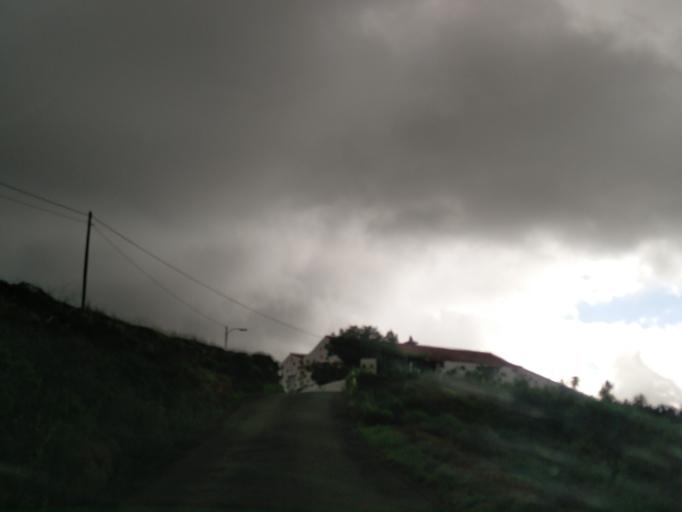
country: ES
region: Canary Islands
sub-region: Provincia de Santa Cruz de Tenerife
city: Arona
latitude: 28.1312
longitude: -16.6921
